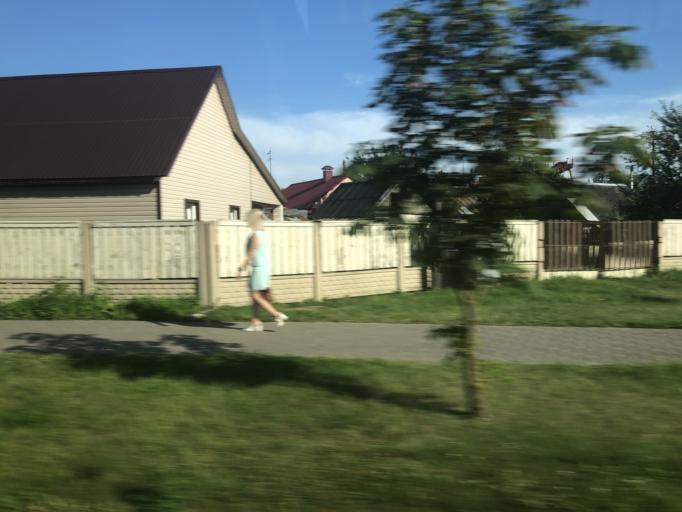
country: BY
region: Grodnenskaya
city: Hrodna
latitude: 53.6606
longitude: 23.8142
